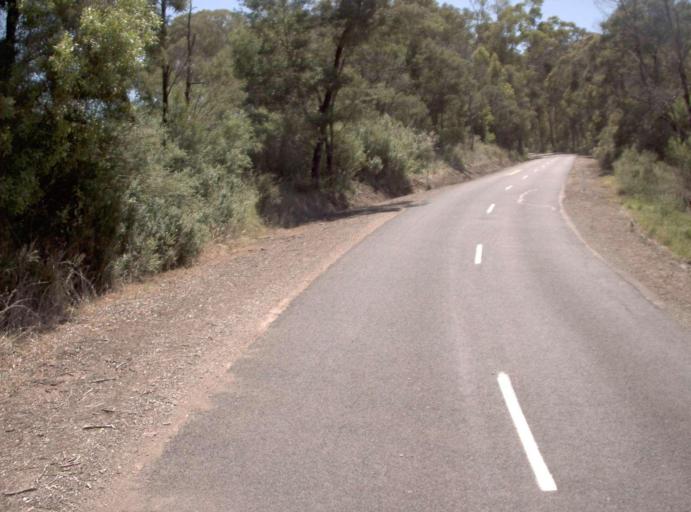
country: AU
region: Victoria
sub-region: East Gippsland
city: Lakes Entrance
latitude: -37.4033
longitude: 148.2117
